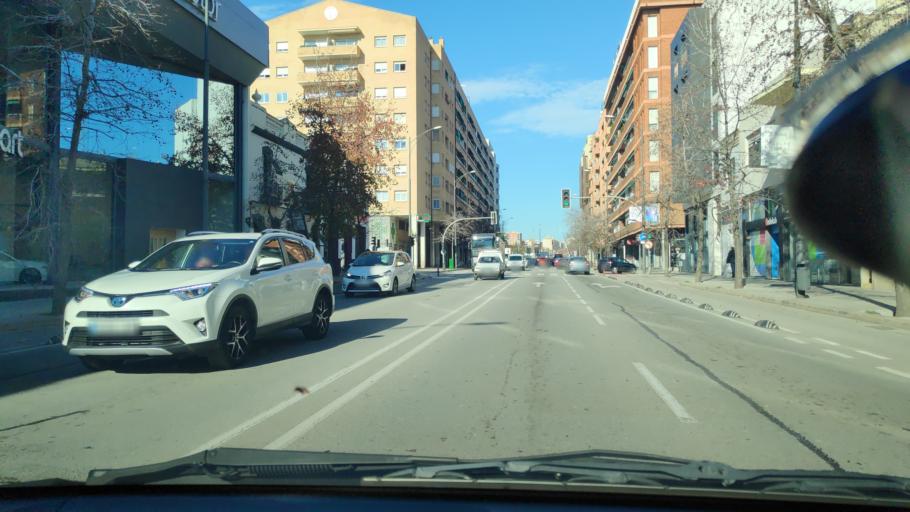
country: ES
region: Catalonia
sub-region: Provincia de Barcelona
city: Sabadell
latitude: 41.5480
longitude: 2.0990
